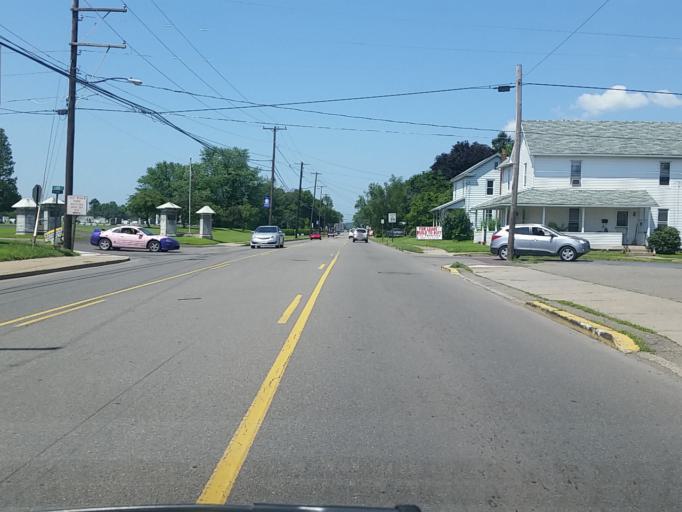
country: US
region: Pennsylvania
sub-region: Columbia County
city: Berwick
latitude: 41.0487
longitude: -76.2605
